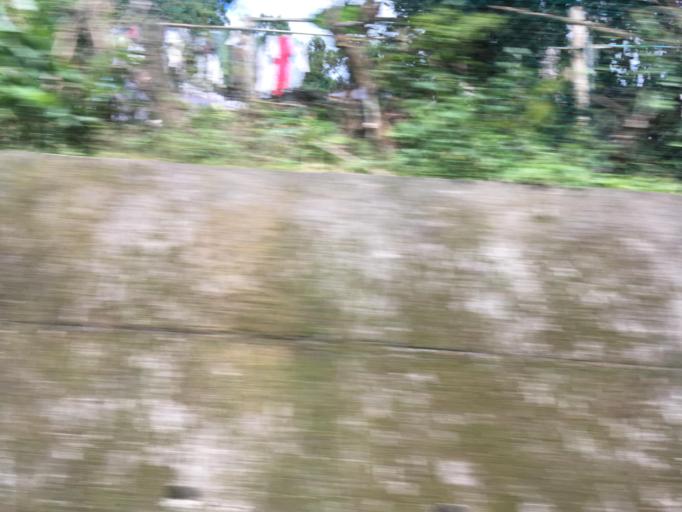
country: TW
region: Taiwan
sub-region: Yilan
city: Yilan
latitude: 24.7540
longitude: 121.6349
